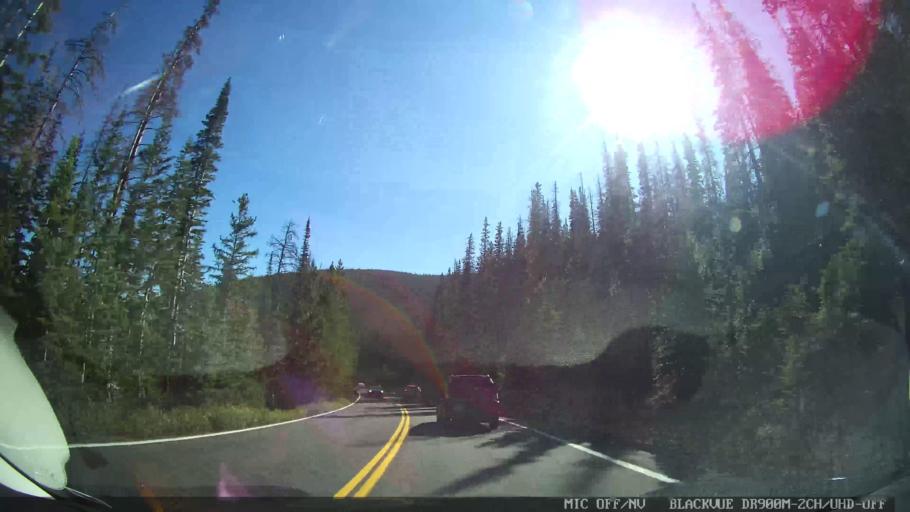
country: US
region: Colorado
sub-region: Larimer County
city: Estes Park
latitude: 40.3866
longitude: -105.6585
